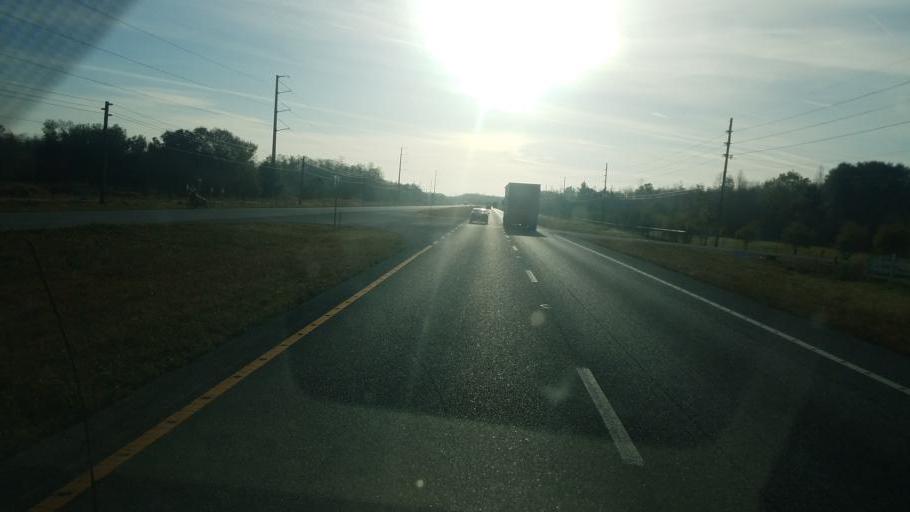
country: US
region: Florida
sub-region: Osceola County
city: Saint Cloud
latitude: 28.1491
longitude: -81.0994
